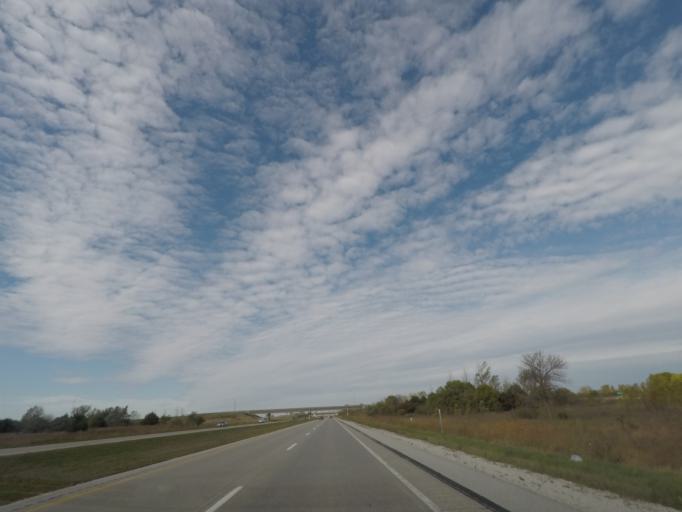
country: US
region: Iowa
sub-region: Story County
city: Ames
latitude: 42.0196
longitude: -93.7153
